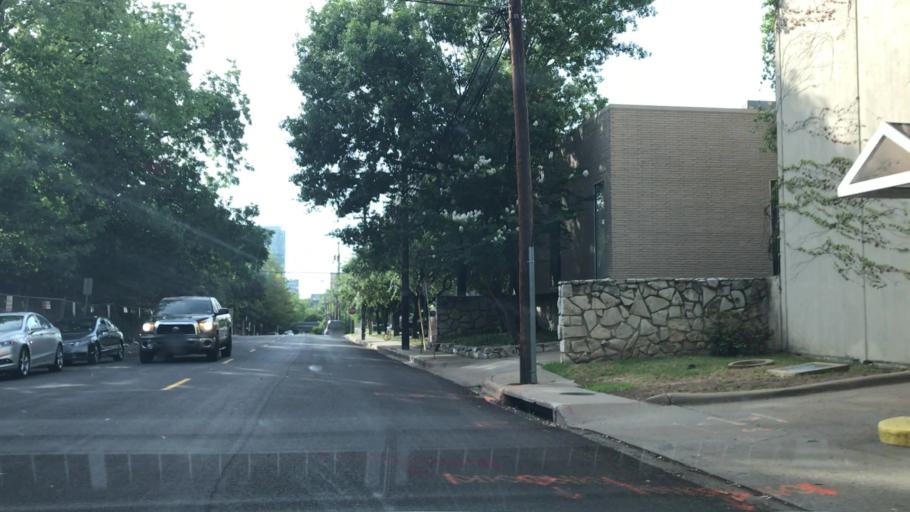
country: US
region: Texas
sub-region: Dallas County
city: Dallas
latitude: 32.7987
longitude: -96.8064
